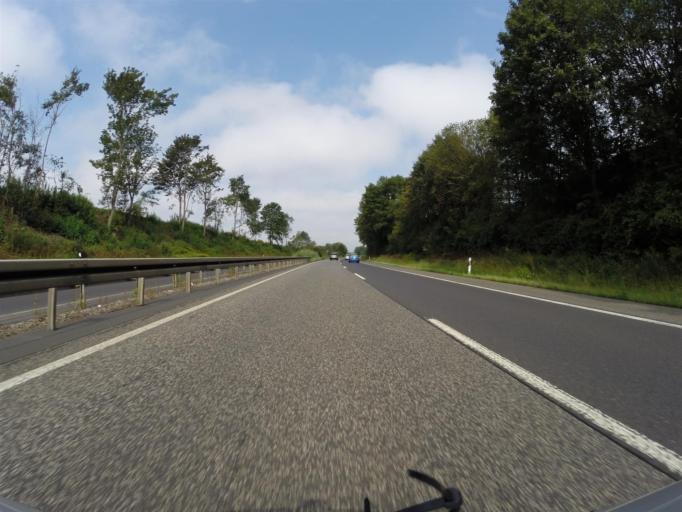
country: DE
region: Hesse
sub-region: Regierungsbezirk Kassel
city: Kaufungen
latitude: 51.2803
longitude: 9.5945
